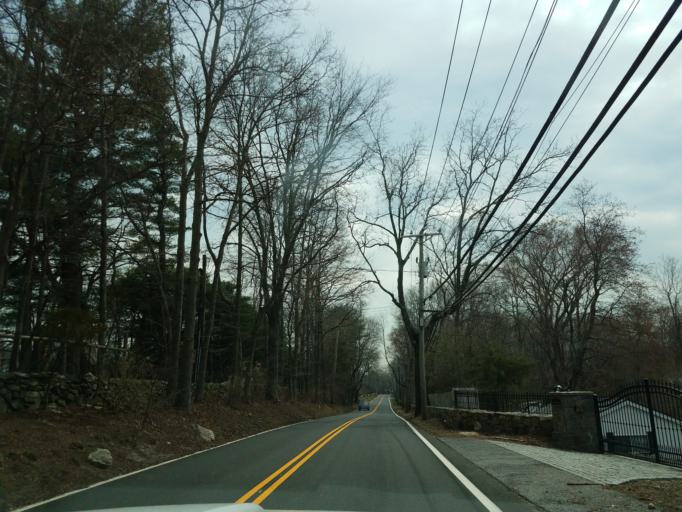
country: US
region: Connecticut
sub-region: Fairfield County
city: Glenville
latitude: 41.0873
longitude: -73.6473
